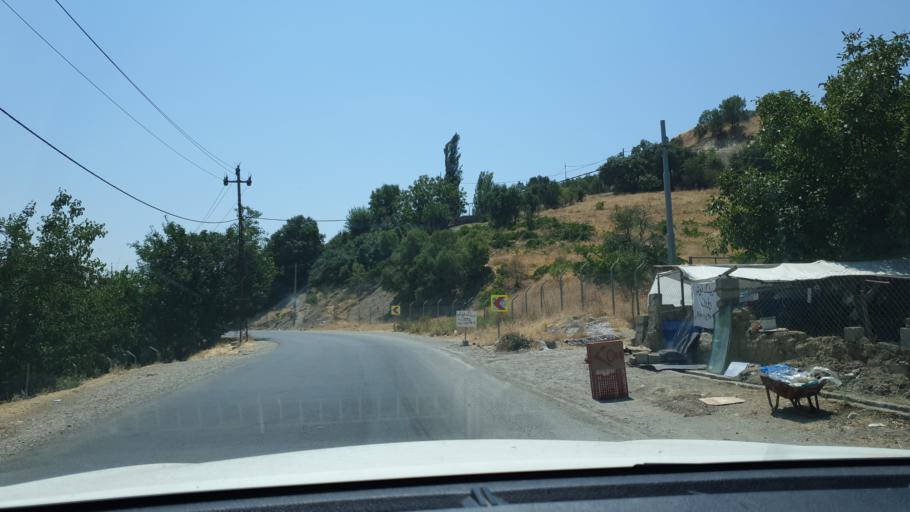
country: IQ
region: Arbil
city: Nahiyat Hiran
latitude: 36.2937
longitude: 44.4758
